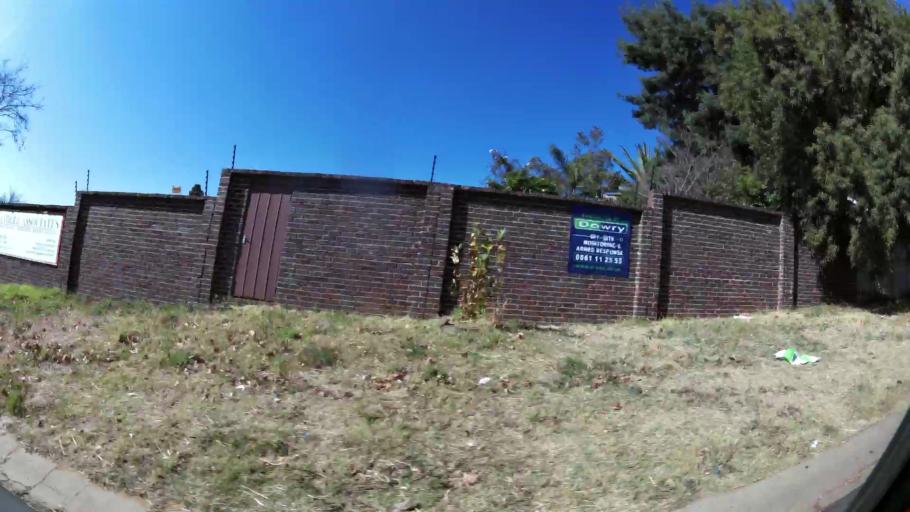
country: ZA
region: Gauteng
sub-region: City of Johannesburg Metropolitan Municipality
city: Roodepoort
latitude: -26.1373
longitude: 27.9107
